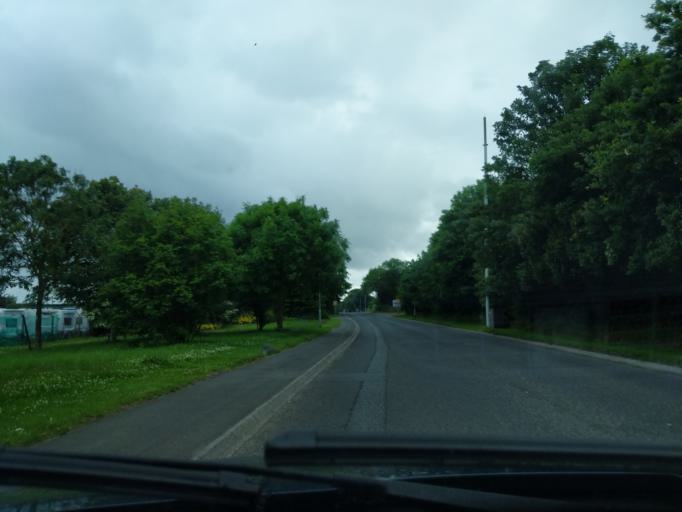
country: GB
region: England
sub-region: Northumberland
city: Seaton Delaval
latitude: 55.0796
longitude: -1.5319
